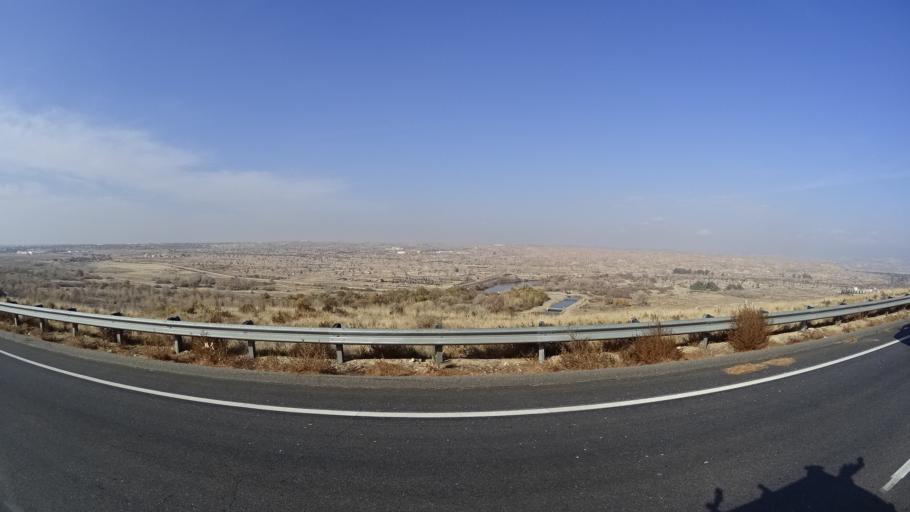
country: US
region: California
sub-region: Kern County
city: Oildale
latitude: 35.4103
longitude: -118.9750
